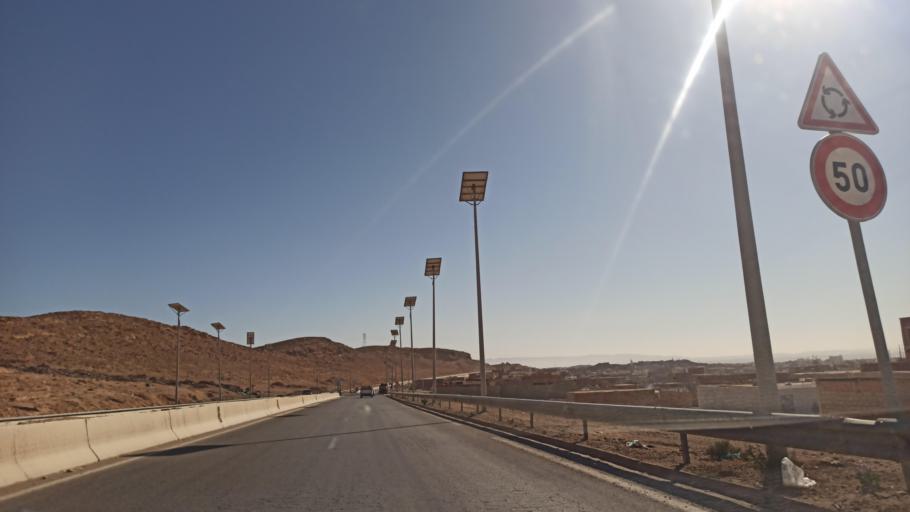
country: TN
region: Gafsa
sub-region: Gafsa Municipality
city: Gafsa
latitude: 34.4459
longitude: 8.7871
